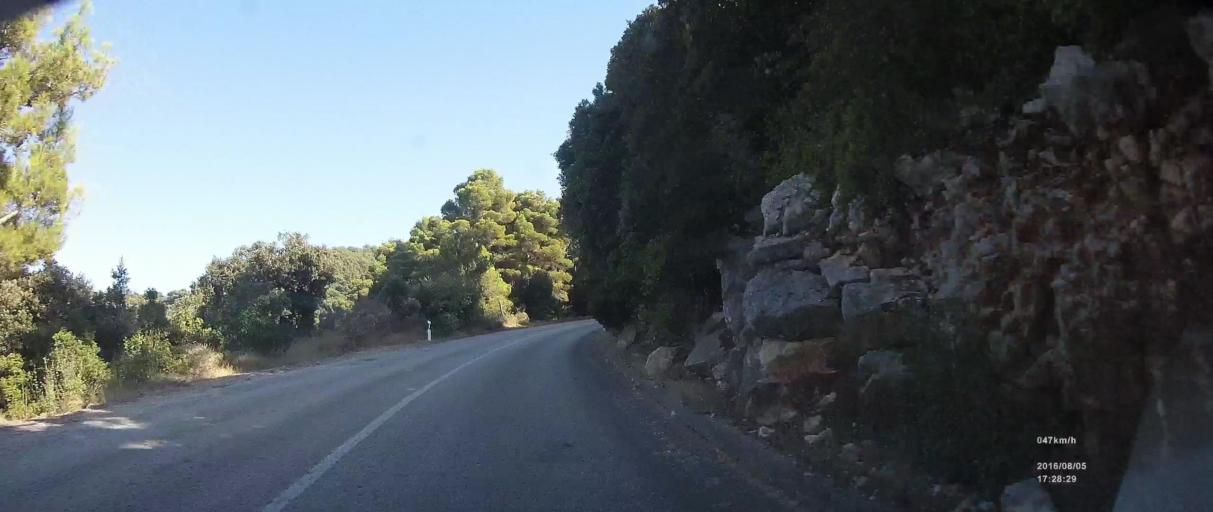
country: HR
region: Dubrovacko-Neretvanska
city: Blato
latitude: 42.7837
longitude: 17.4056
